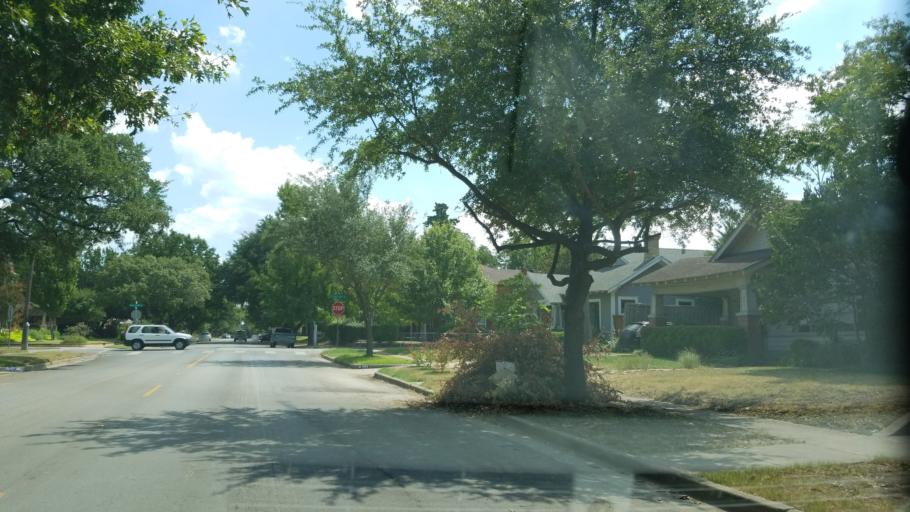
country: US
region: Texas
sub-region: Dallas County
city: Cockrell Hill
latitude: 32.7532
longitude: -96.8440
